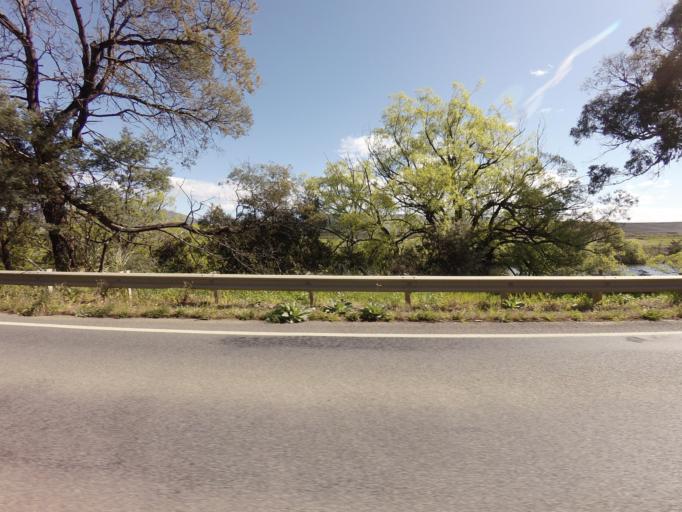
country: AU
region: Tasmania
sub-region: Derwent Valley
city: New Norfolk
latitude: -42.7426
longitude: 146.9848
